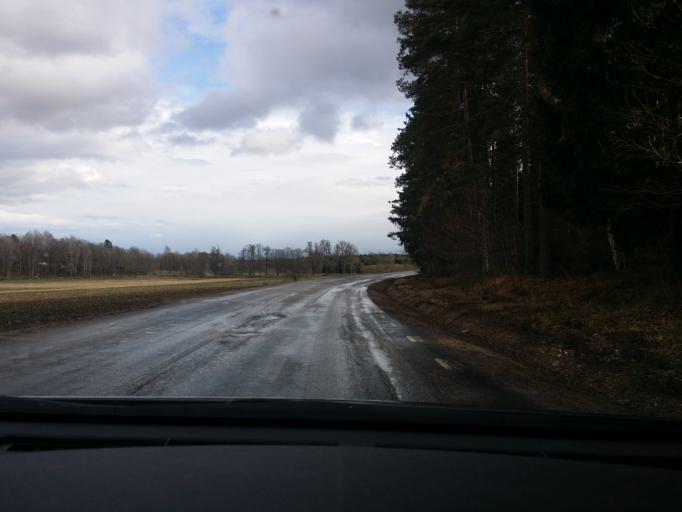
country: SE
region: Soedermanland
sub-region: Eskilstuna Kommun
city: Arla
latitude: 59.3107
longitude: 16.6816
